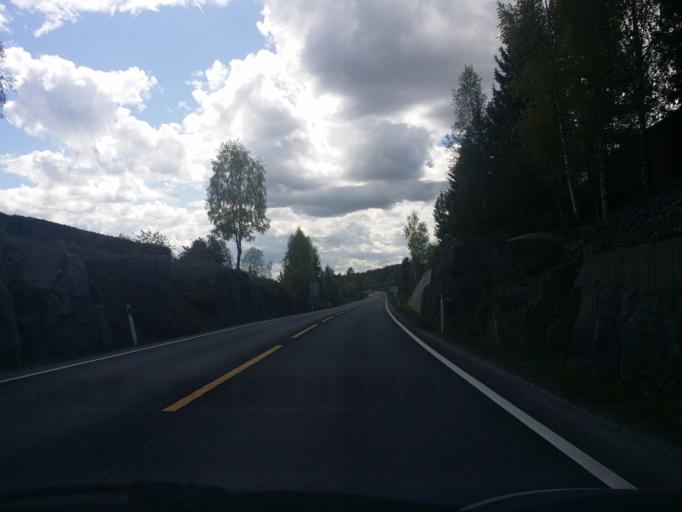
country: NO
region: Buskerud
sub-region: Modum
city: Vikersund
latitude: 59.9690
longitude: 9.9860
